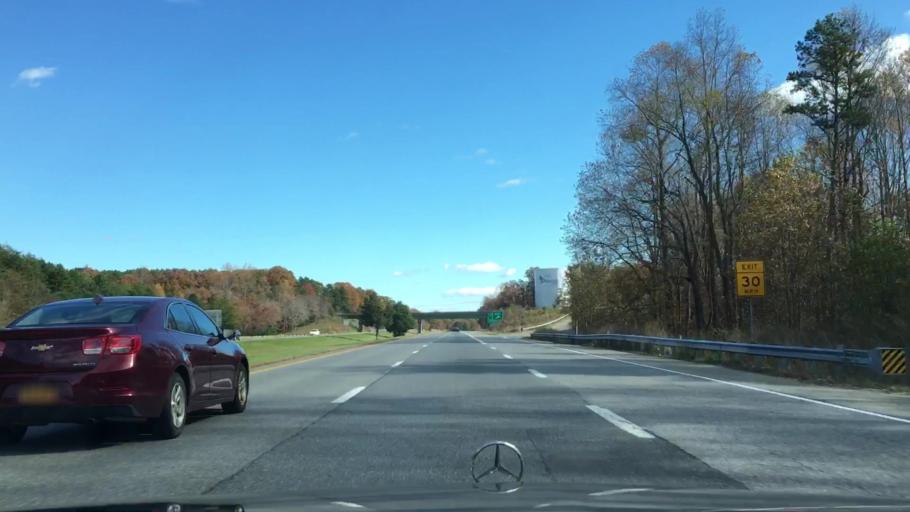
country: US
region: Virginia
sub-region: Campbell County
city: Altavista
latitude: 37.1378
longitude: -79.2727
